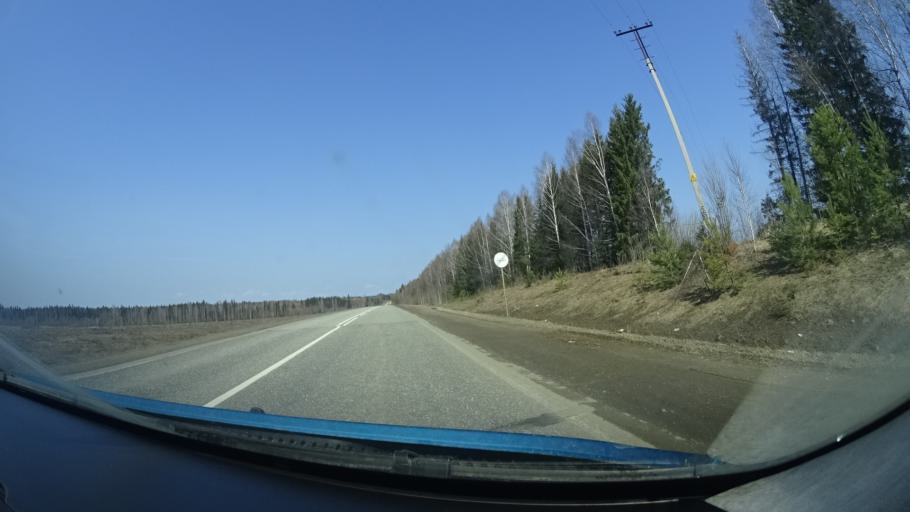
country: RU
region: Perm
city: Osa
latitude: 57.3787
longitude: 55.6095
